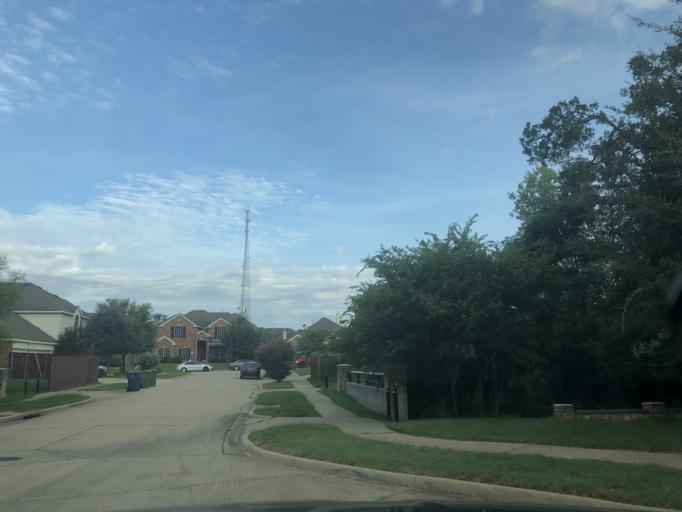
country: US
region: Texas
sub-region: Dallas County
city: Sunnyvale
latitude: 32.8482
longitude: -96.5872
